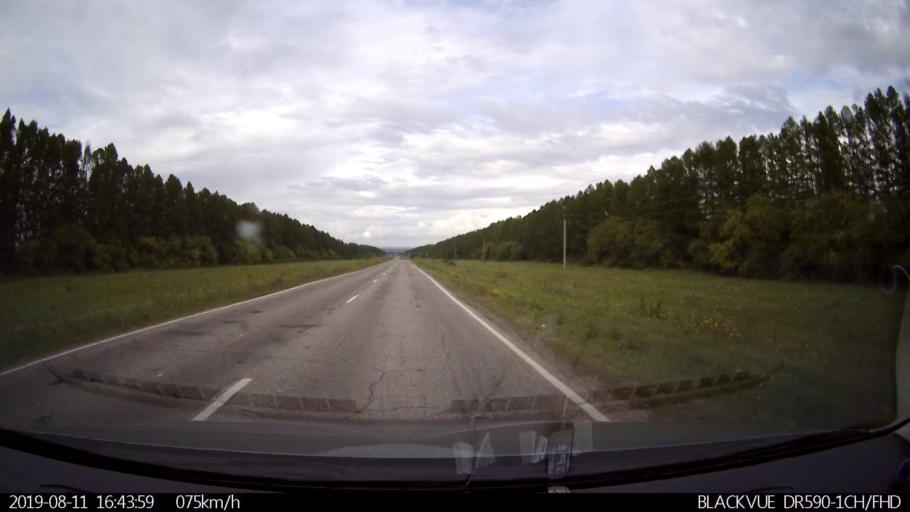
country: RU
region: Ulyanovsk
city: Mayna
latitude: 54.1746
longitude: 47.6772
